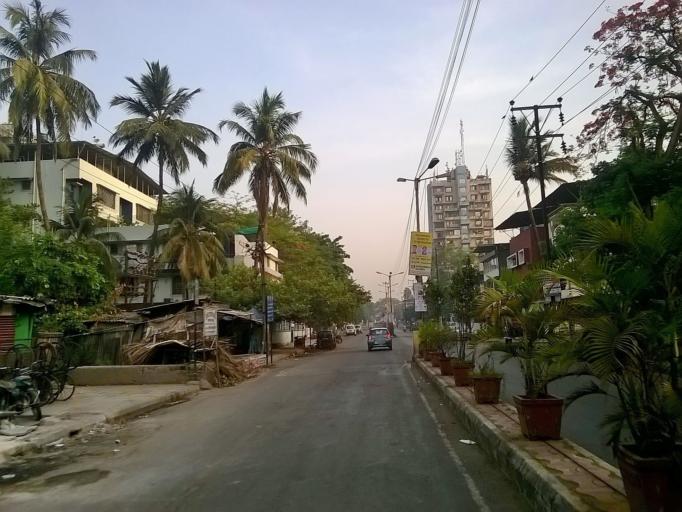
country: IN
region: Maharashtra
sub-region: Raigarh
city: Panvel
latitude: 18.9948
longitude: 73.1197
